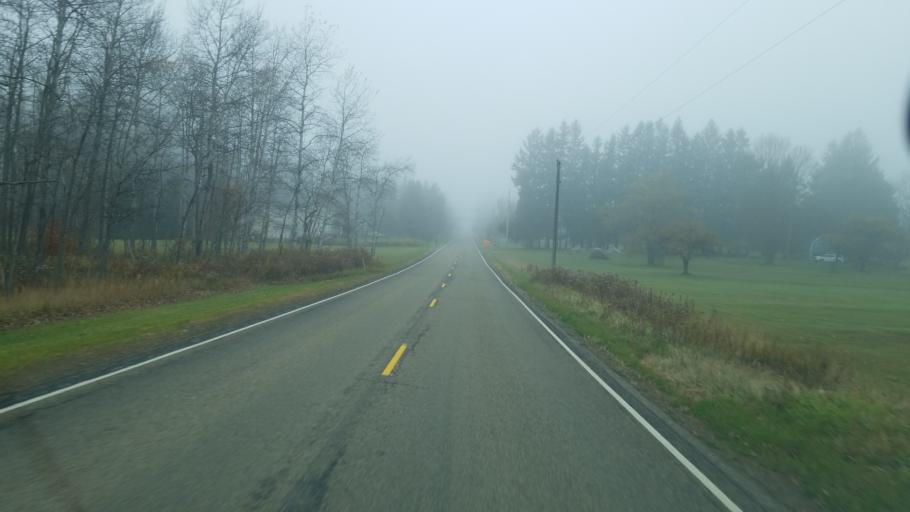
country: US
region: Pennsylvania
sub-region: McKean County
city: Smethport
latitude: 41.8068
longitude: -78.5308
